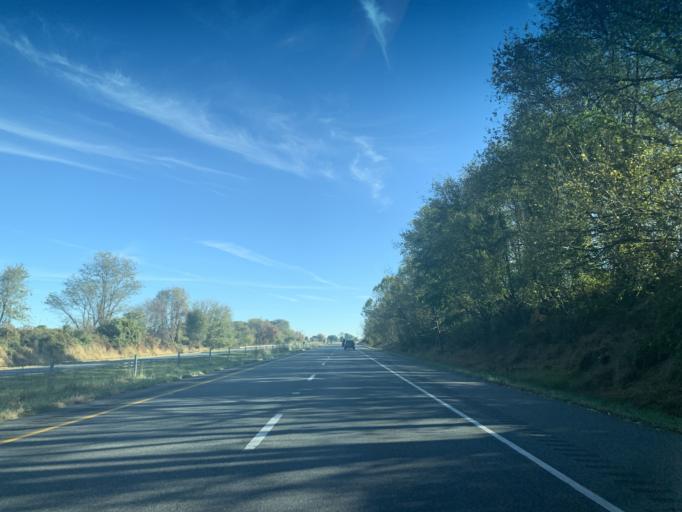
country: US
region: Pennsylvania
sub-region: Chester County
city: Oxford
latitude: 39.8028
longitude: -75.9755
